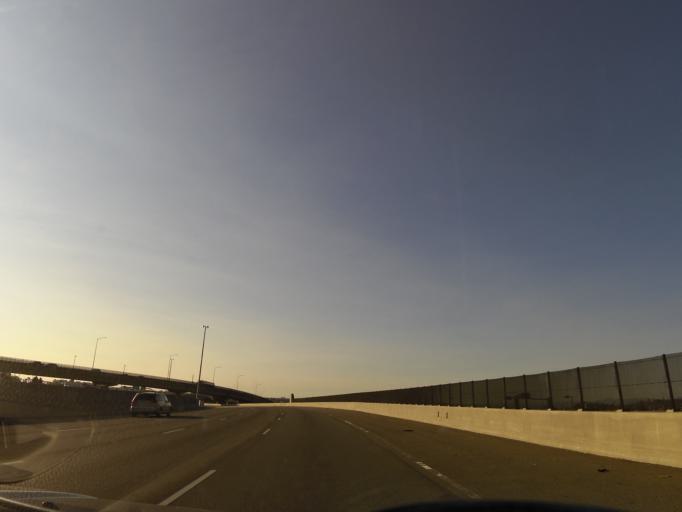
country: US
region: Colorado
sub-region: Denver County
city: Denver
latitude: 39.7069
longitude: -104.9970
